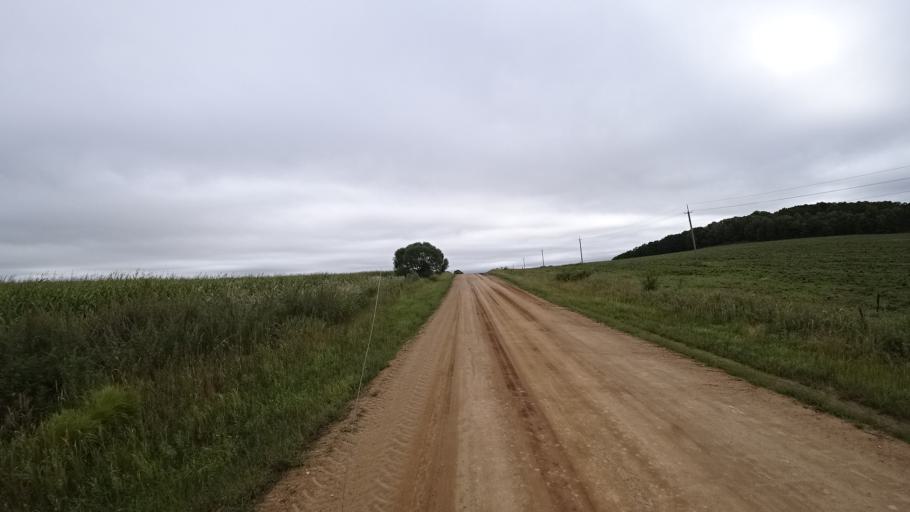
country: RU
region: Primorskiy
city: Monastyrishche
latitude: 44.0925
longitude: 132.5995
